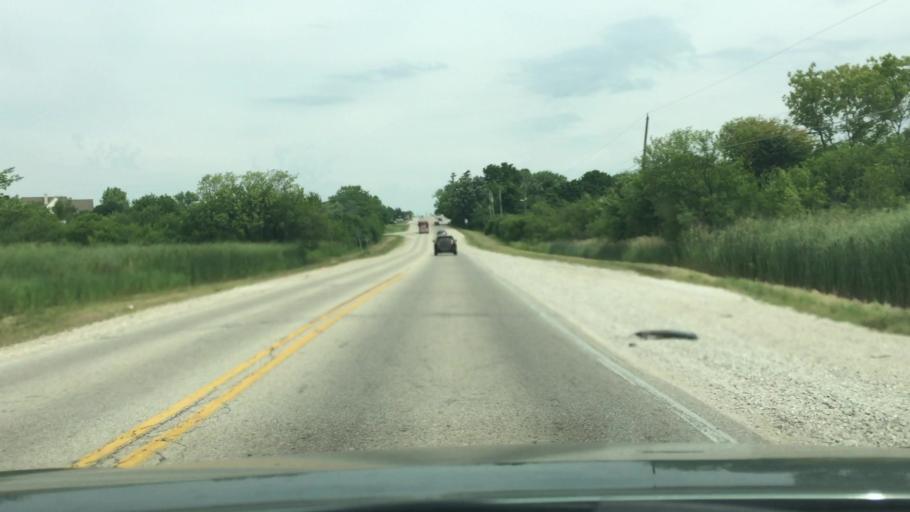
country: US
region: Wisconsin
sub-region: Waukesha County
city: Hartland
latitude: 43.0991
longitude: -88.3135
